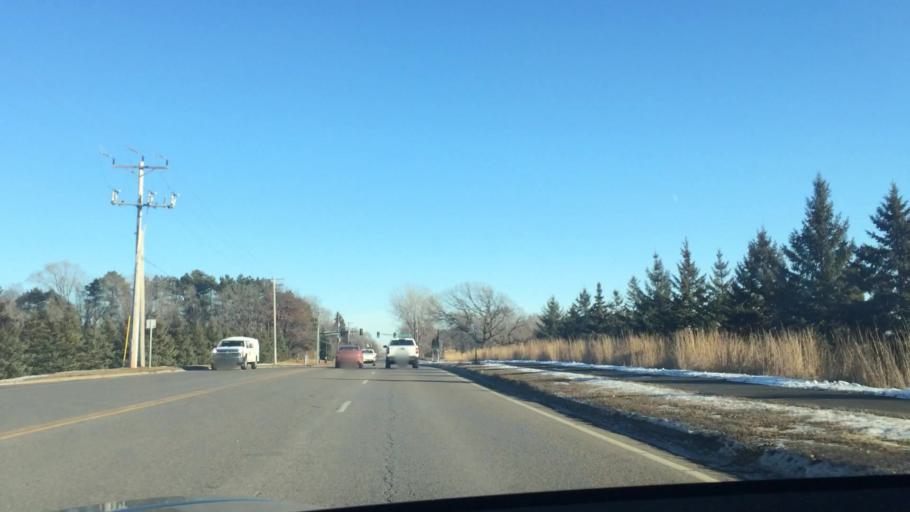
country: US
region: Minnesota
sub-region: Anoka County
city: Lexington
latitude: 45.1243
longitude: -93.1761
